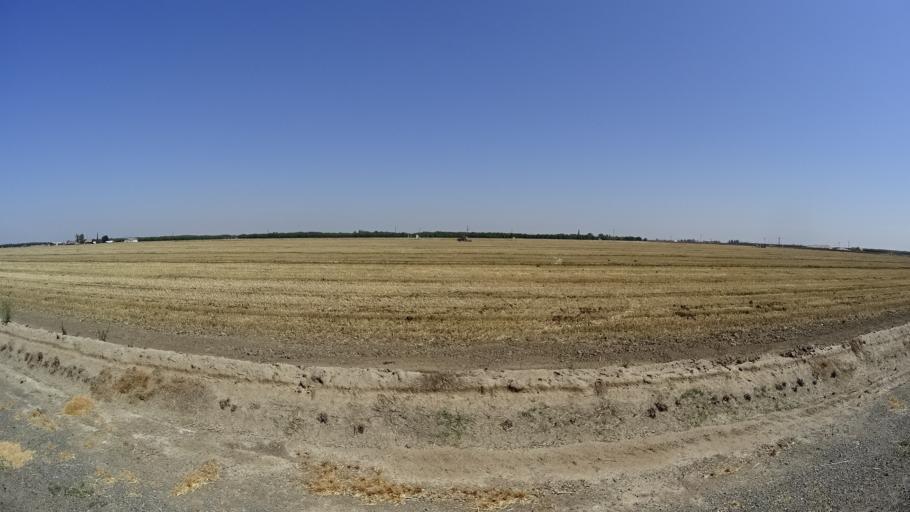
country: US
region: California
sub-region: Kings County
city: Lucerne
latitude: 36.3717
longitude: -119.7039
